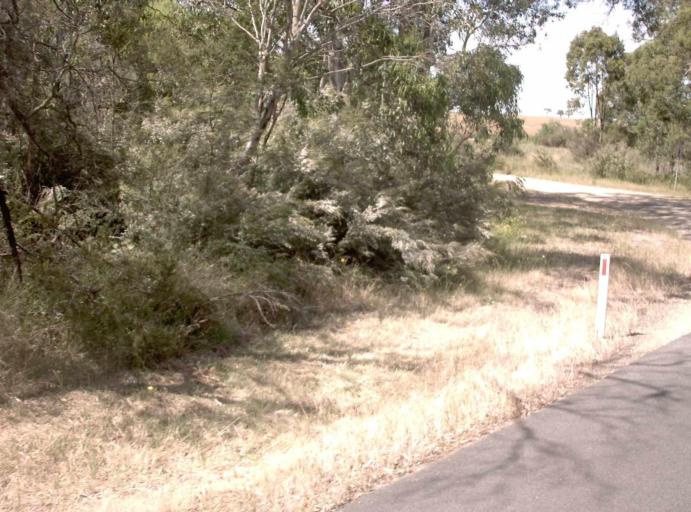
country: AU
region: Victoria
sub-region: Wellington
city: Sale
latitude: -37.9362
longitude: 147.1639
